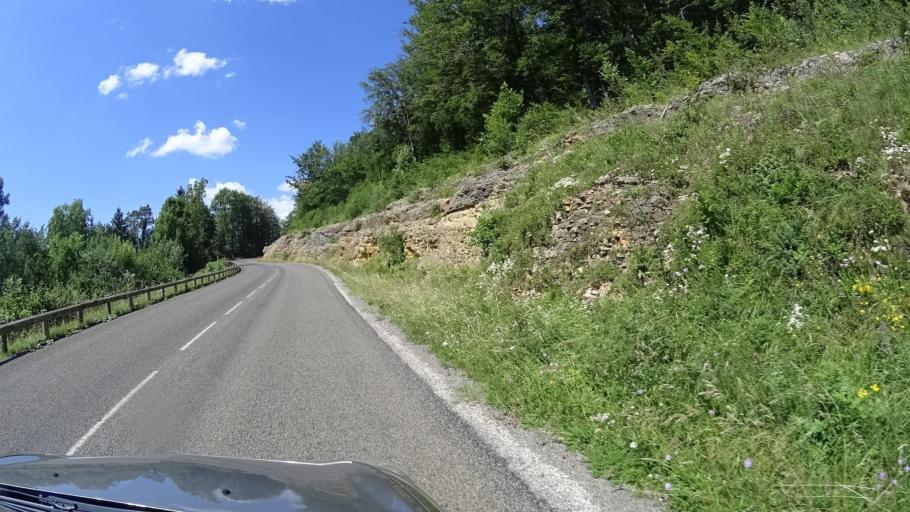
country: FR
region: Franche-Comte
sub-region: Departement du Jura
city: Longchaumois
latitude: 46.5048
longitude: 5.9484
